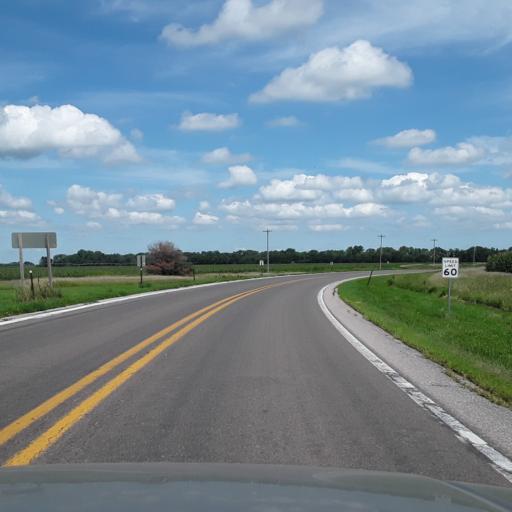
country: US
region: Nebraska
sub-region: Polk County
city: Osceola
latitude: 41.0774
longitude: -97.4247
